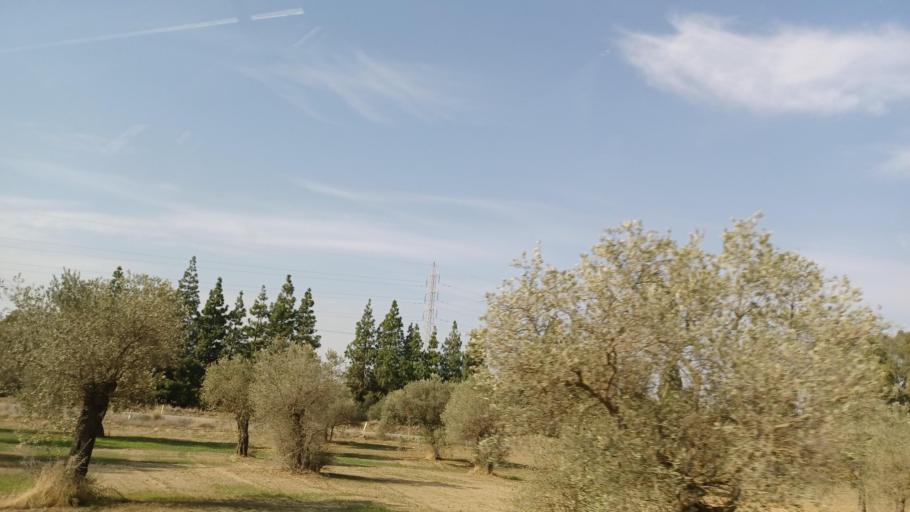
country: CY
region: Larnaka
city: Mosfiloti
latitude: 34.9663
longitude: 33.4132
